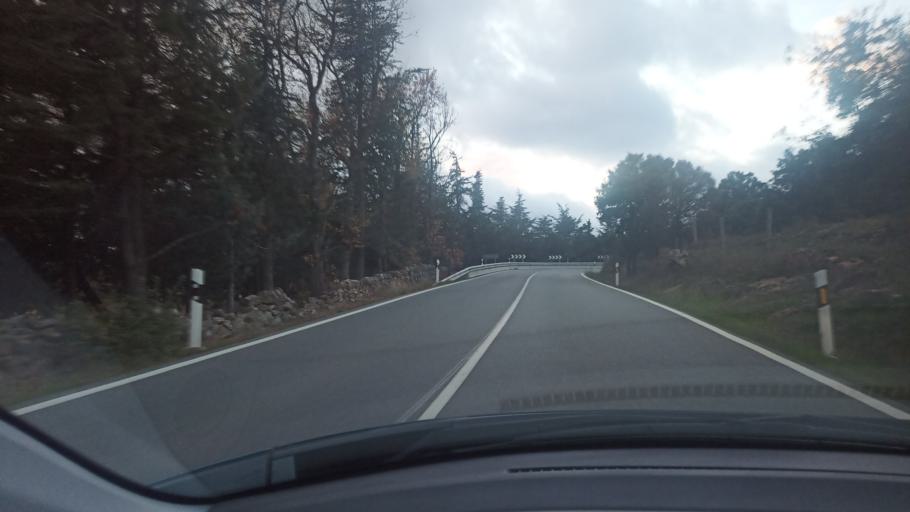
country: ES
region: Madrid
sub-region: Provincia de Madrid
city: El Escorial
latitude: 40.5374
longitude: -4.1336
